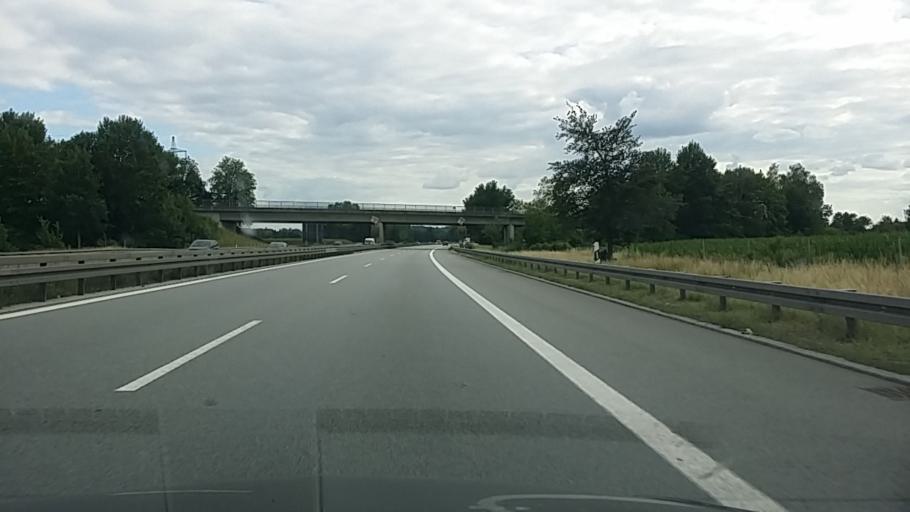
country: DE
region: Bavaria
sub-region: Lower Bavaria
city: Eching
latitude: 48.5269
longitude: 12.0693
